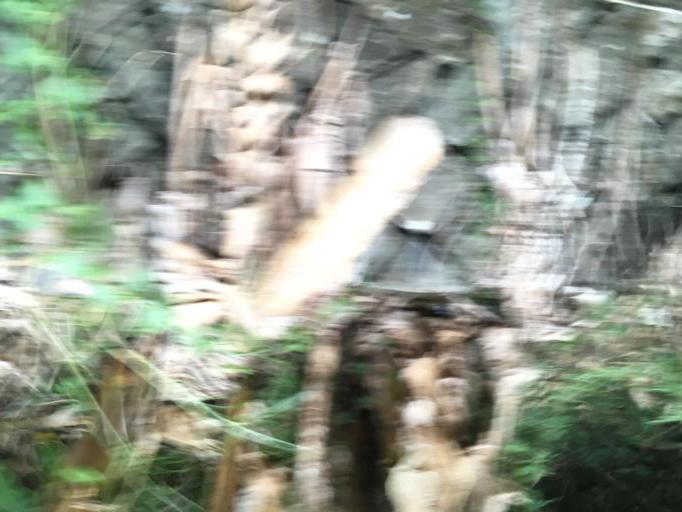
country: TW
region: Taiwan
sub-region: Chiayi
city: Jiayi Shi
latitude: 23.5340
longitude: 120.5856
